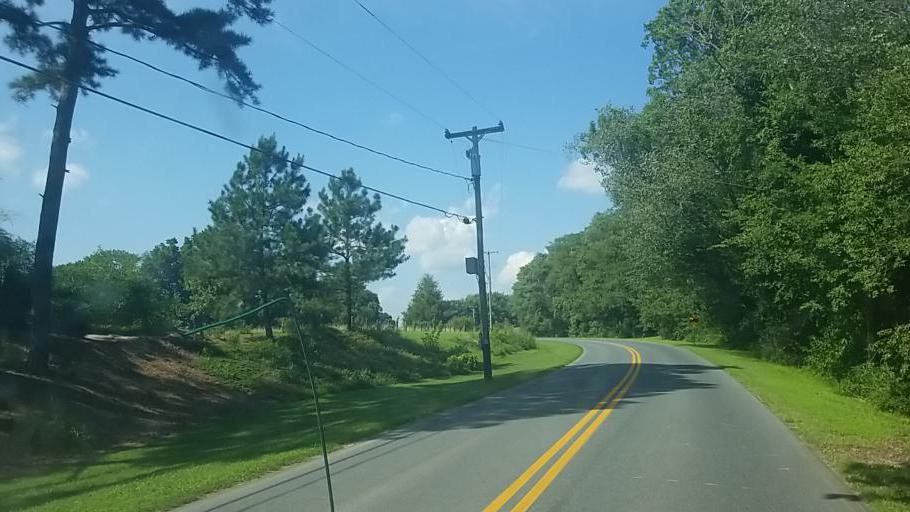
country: US
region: Maryland
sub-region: Somerset County
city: Princess Anne
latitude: 38.2648
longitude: -75.6804
